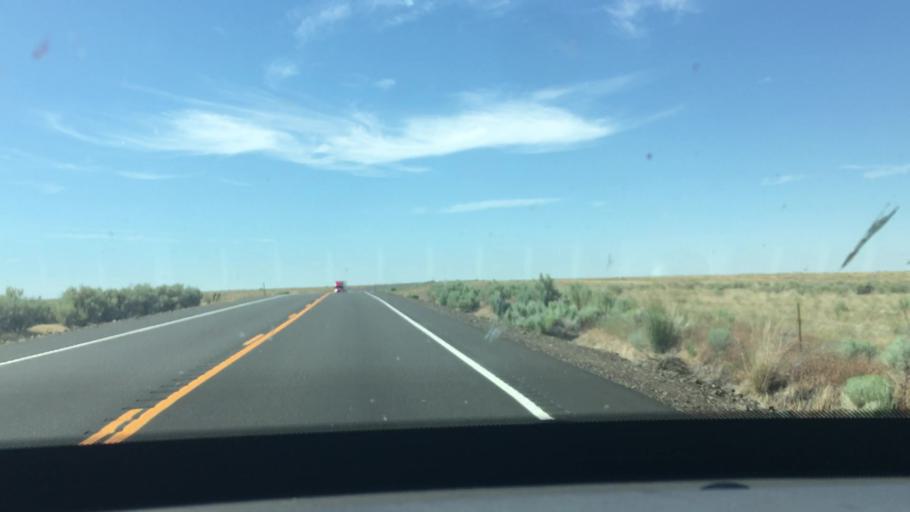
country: US
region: Oregon
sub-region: Sherman County
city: Moro
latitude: 45.1081
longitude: -120.6841
